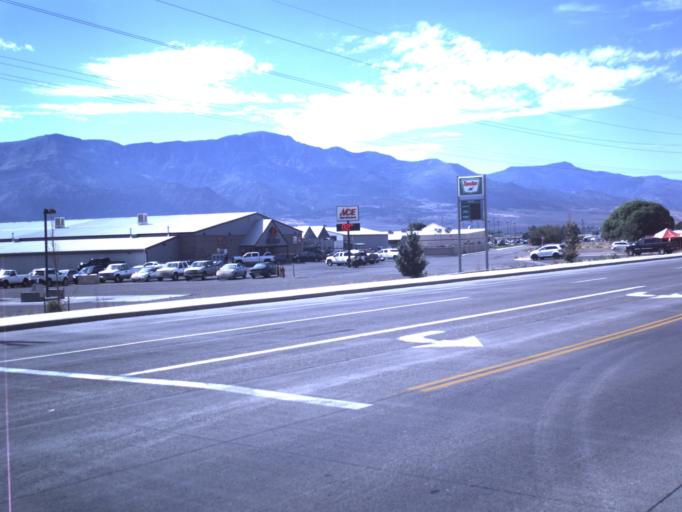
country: US
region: Utah
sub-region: Sevier County
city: Richfield
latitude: 38.7532
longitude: -112.0863
